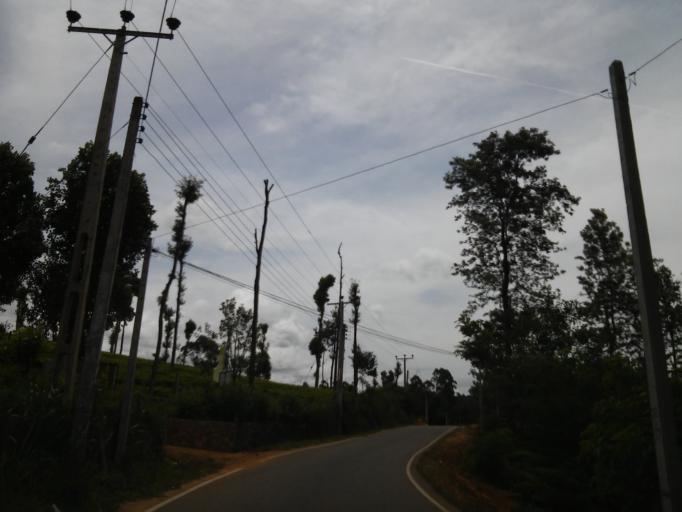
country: LK
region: Uva
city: Haputale
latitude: 6.8489
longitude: 81.0237
